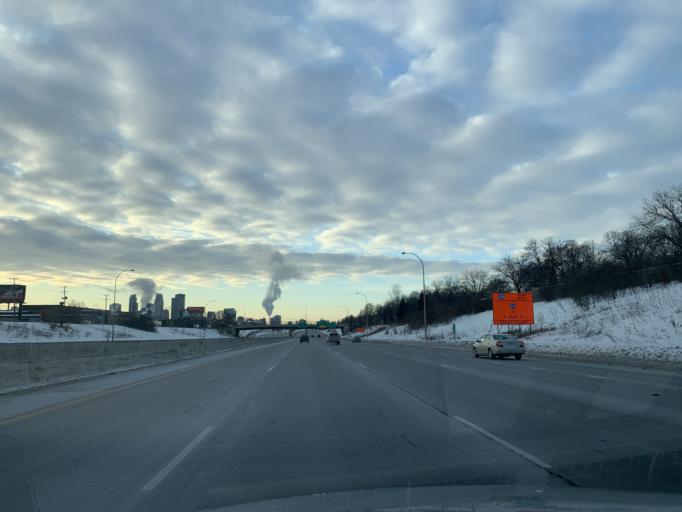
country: US
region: Minnesota
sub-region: Hennepin County
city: Minneapolis
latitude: 45.0089
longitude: -93.2828
